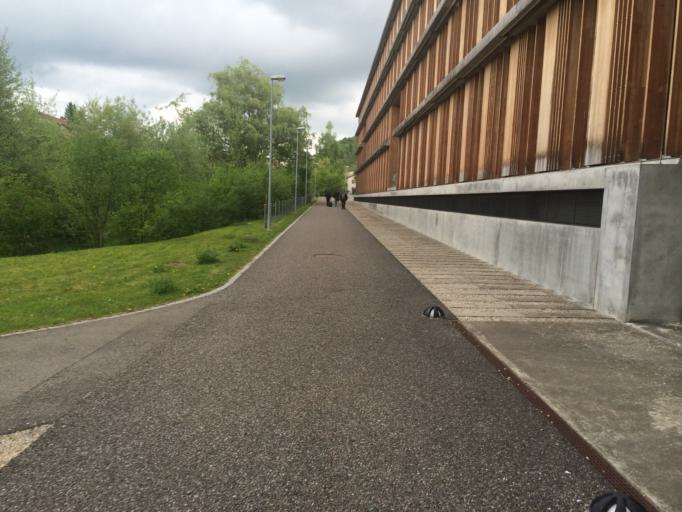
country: CH
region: Bern
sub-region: Bern-Mittelland District
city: Bolligen
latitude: 46.9758
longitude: 7.4734
